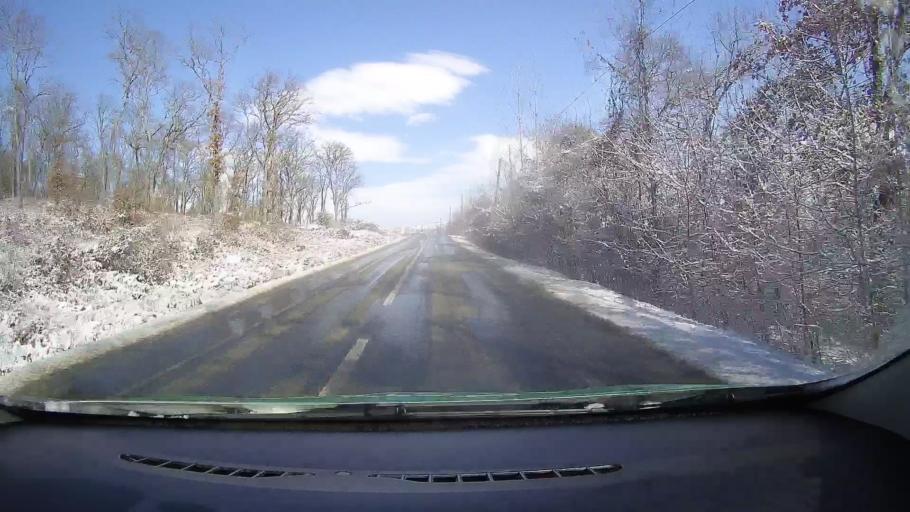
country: RO
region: Sibiu
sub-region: Comuna Nocrich
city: Nocrich
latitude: 45.8614
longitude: 24.4529
